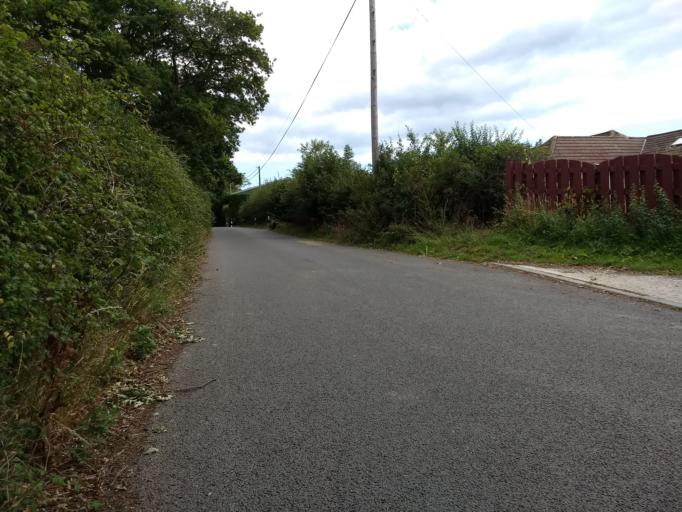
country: GB
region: England
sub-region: Isle of Wight
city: Ryde
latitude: 50.7088
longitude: -1.1801
